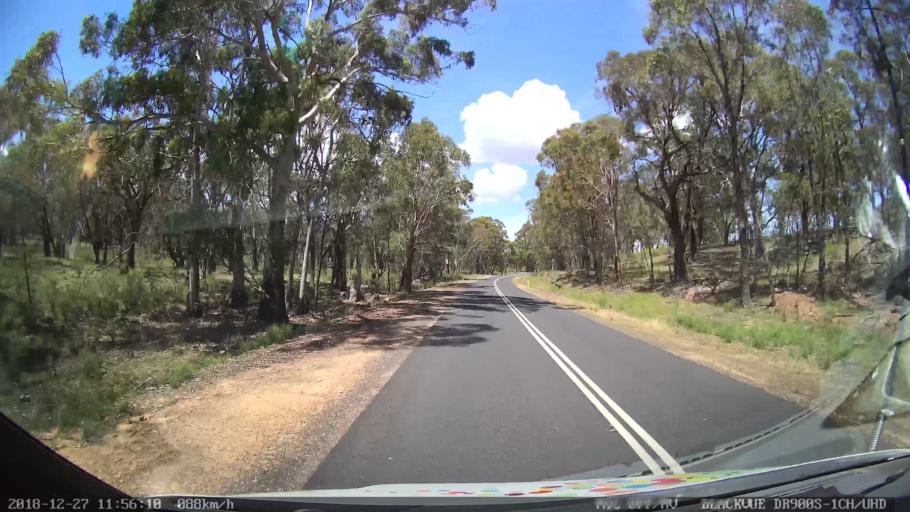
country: AU
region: New South Wales
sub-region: Blayney
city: Blayney
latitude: -33.6953
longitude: 149.3936
